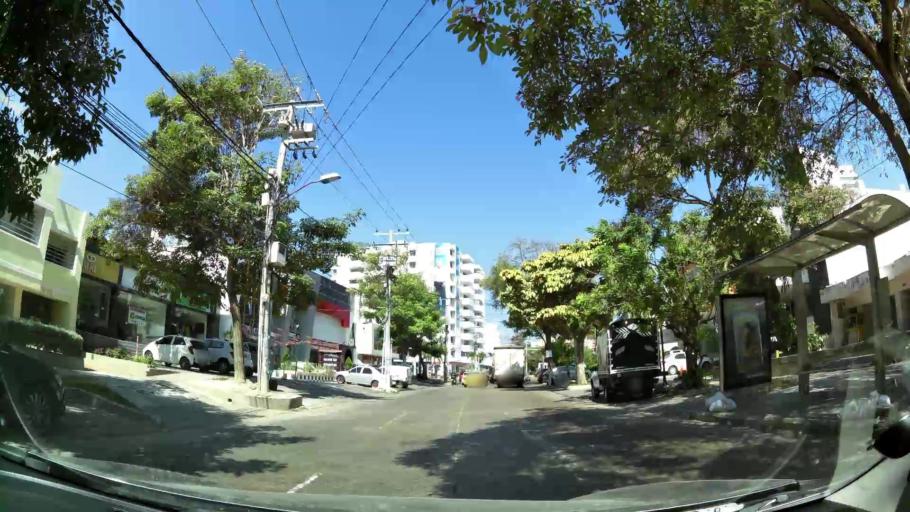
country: CO
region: Atlantico
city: Barranquilla
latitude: 10.9978
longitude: -74.8020
